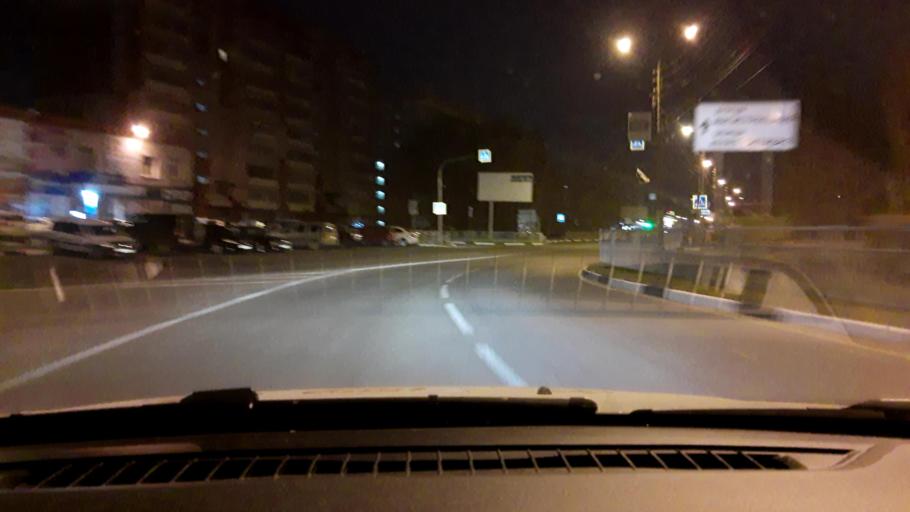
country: RU
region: Nizjnij Novgorod
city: Kstovo
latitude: 56.1555
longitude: 44.2134
